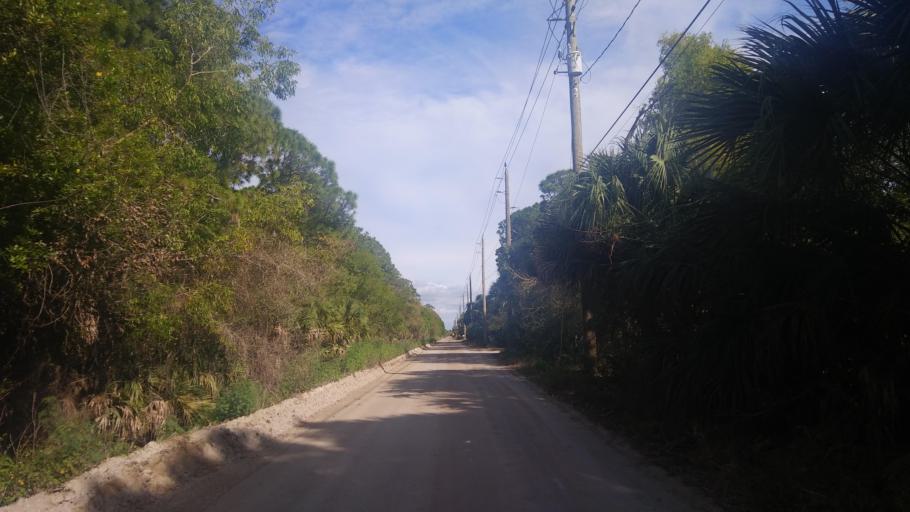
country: US
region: Florida
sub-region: Indian River County
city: Fellsmere
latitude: 27.7500
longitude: -80.5917
